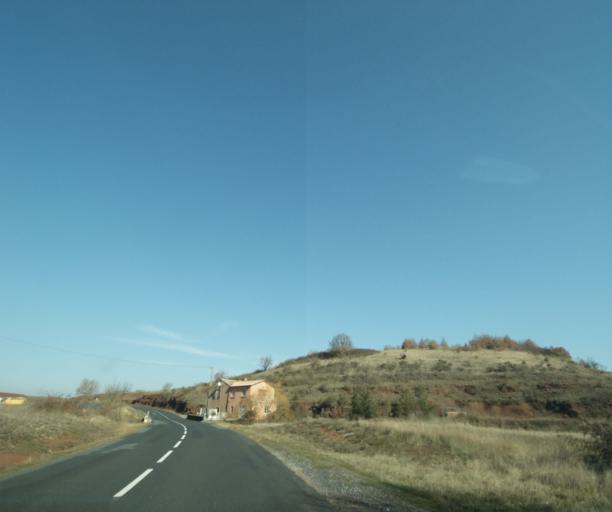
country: FR
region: Midi-Pyrenees
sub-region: Departement de l'Aveyron
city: Camares
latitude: 43.8572
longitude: 2.8305
